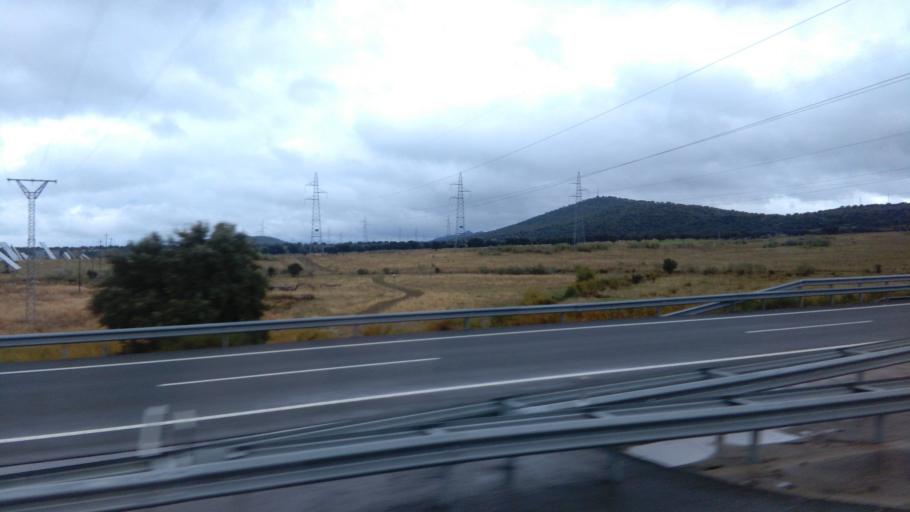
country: ES
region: Extremadura
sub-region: Provincia de Caceres
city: Almaraz
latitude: 39.8211
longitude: -5.6616
